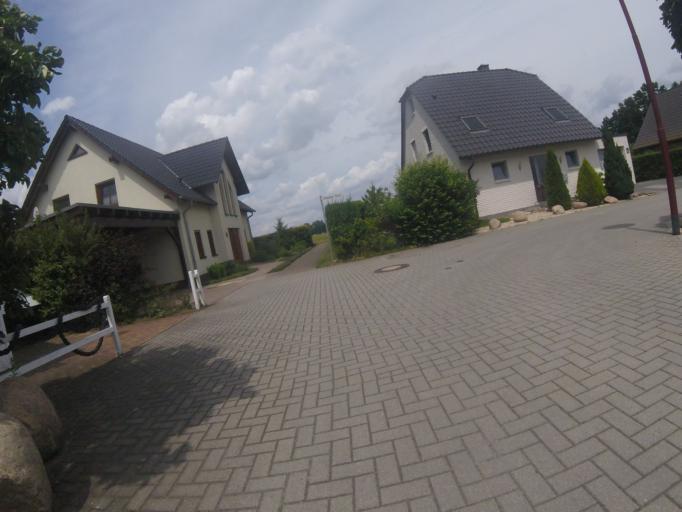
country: DE
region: Brandenburg
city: Konigs Wusterhausen
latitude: 52.2840
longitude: 13.6065
